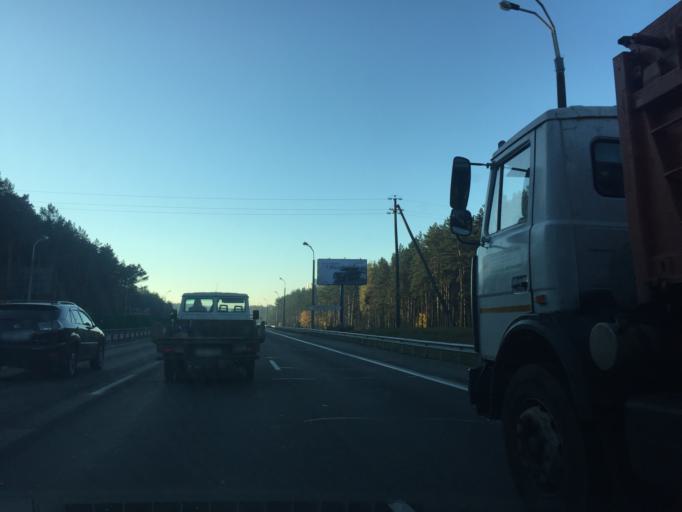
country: BY
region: Minsk
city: Vyaliki Trastsyanets
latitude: 53.8956
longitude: 27.6916
